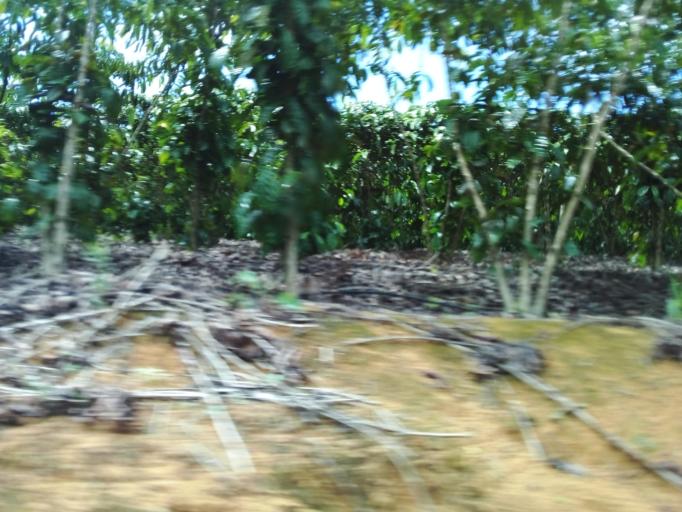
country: BR
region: Espirito Santo
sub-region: Santa Leopoldina
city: Santa Leopoldina
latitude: -20.0665
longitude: -40.4193
